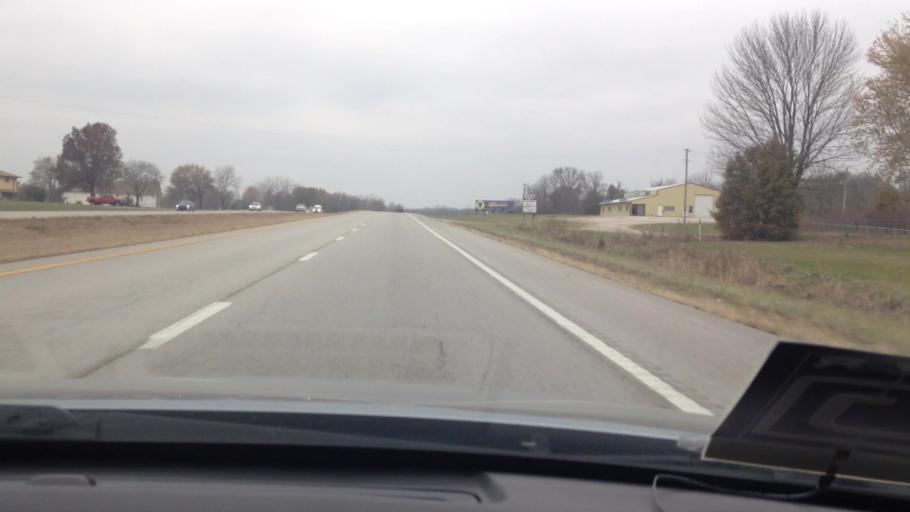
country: US
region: Missouri
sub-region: Cass County
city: Harrisonville
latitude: 38.6117
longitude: -94.3232
